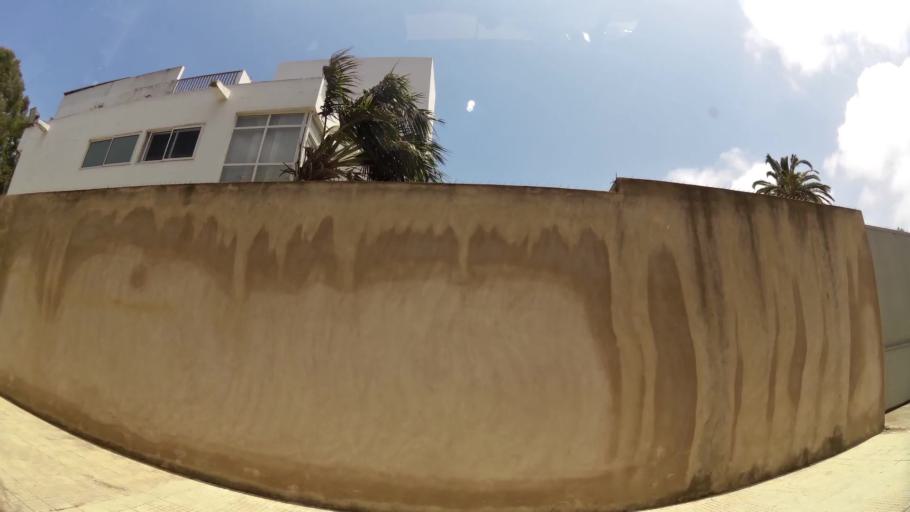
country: MA
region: Rabat-Sale-Zemmour-Zaer
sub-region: Rabat
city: Rabat
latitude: 34.0074
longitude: -6.8473
